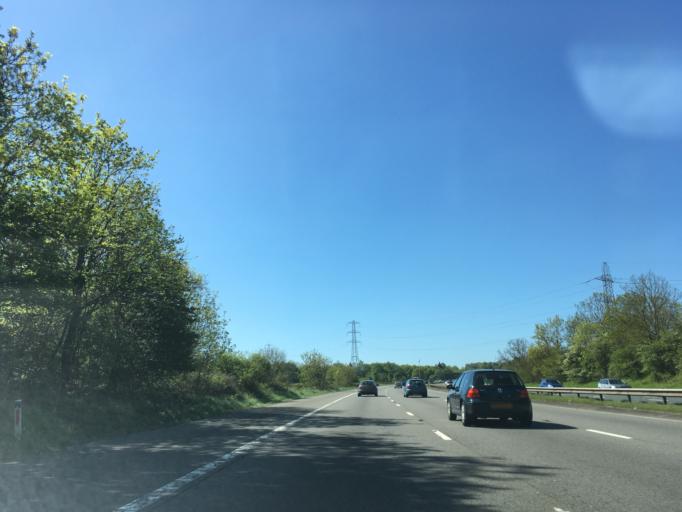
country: GB
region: England
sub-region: South Gloucestershire
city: Tytherington
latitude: 51.6123
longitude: -2.4649
